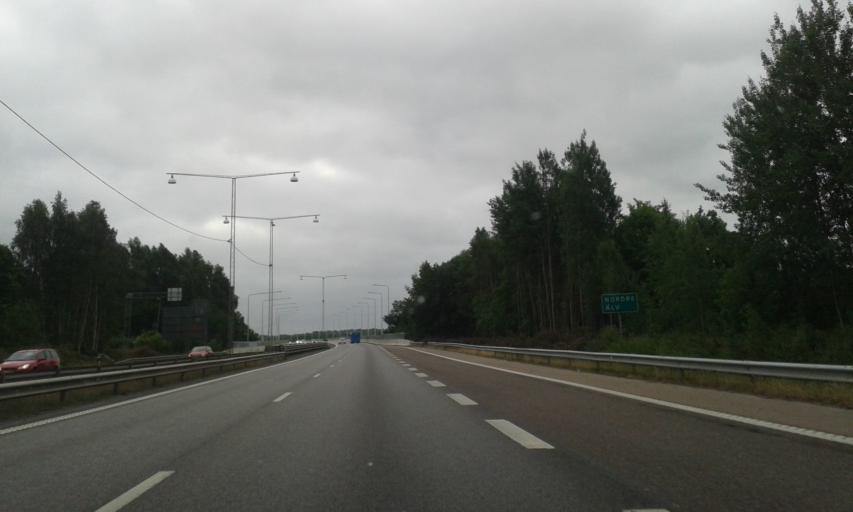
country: SE
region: Vaestra Goetaland
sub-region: Kungalvs Kommun
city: Kungalv
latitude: 57.8705
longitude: 11.9679
